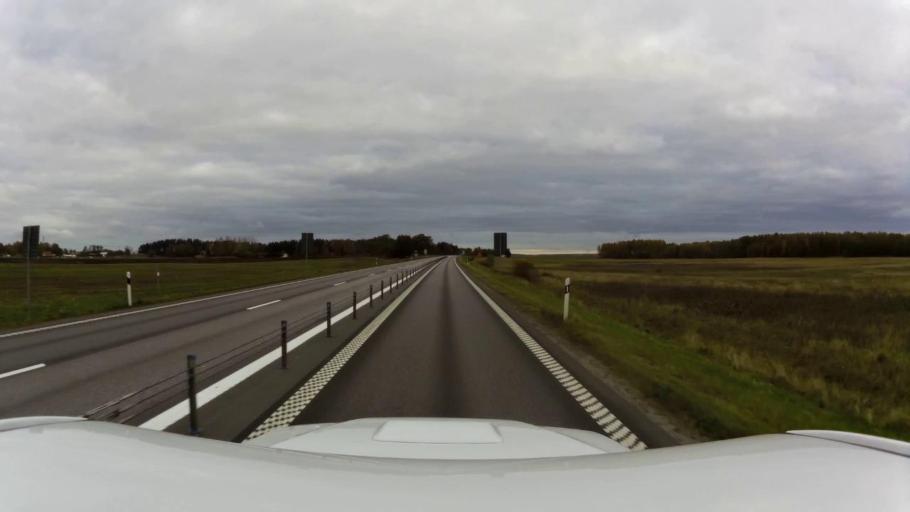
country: SE
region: OEstergoetland
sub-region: Linkopings Kommun
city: Ljungsbro
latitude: 58.4967
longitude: 15.4609
